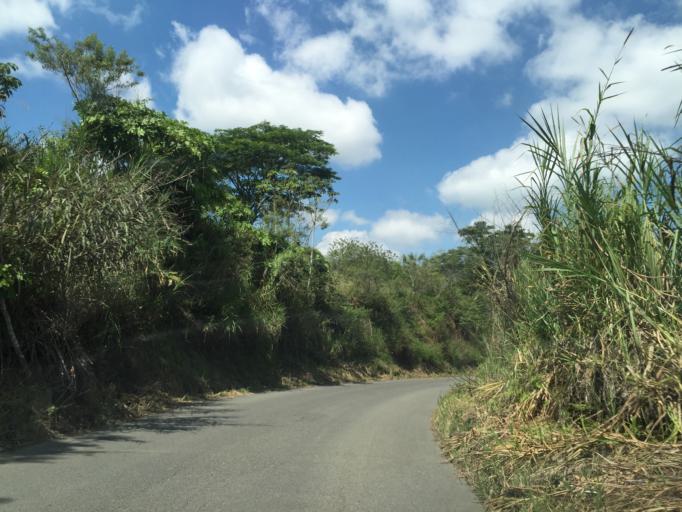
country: CO
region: Valle del Cauca
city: Alcala
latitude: 4.7146
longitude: -75.7945
